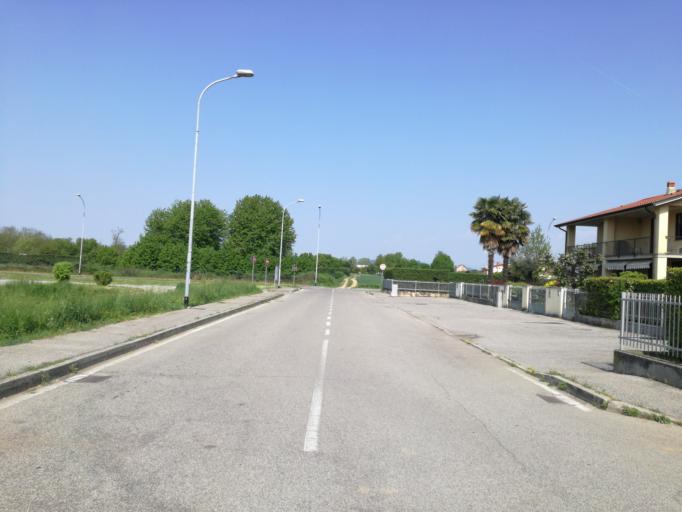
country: IT
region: Lombardy
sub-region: Provincia di Lecco
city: Verderio Inferiore
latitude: 45.6686
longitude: 9.4350
